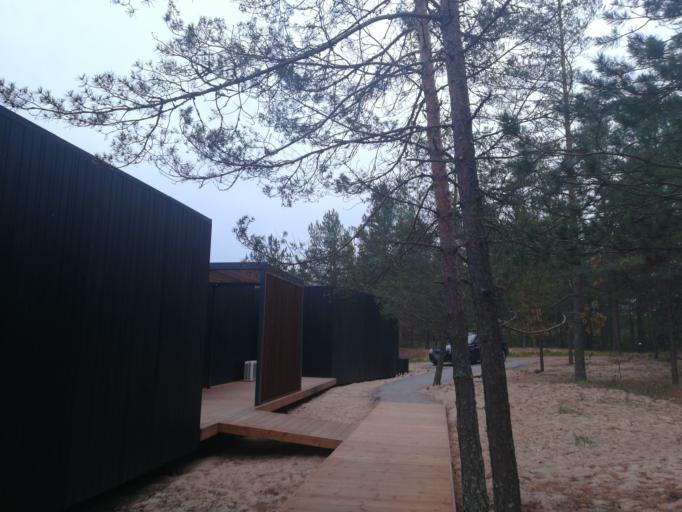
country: RU
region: Leningrad
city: Priozersk
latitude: 61.0423
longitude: 30.1810
